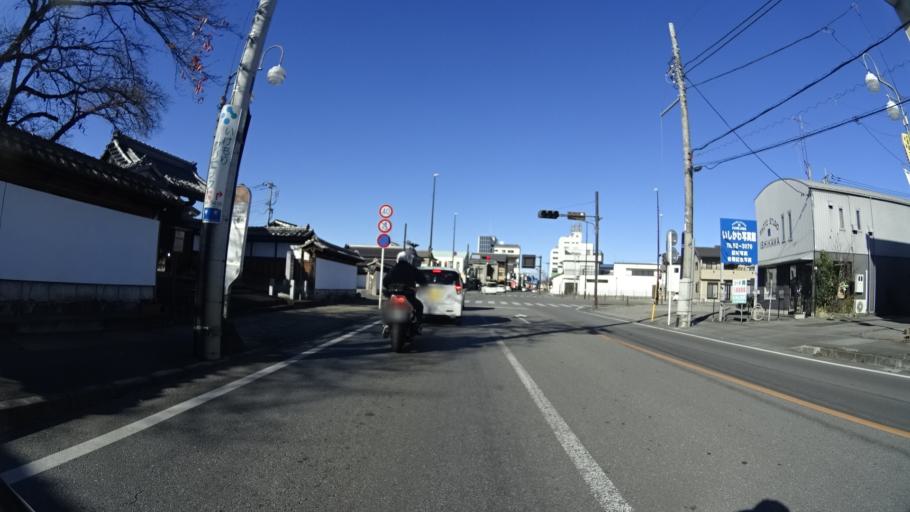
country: JP
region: Tochigi
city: Kanuma
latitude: 36.5610
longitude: 139.7466
